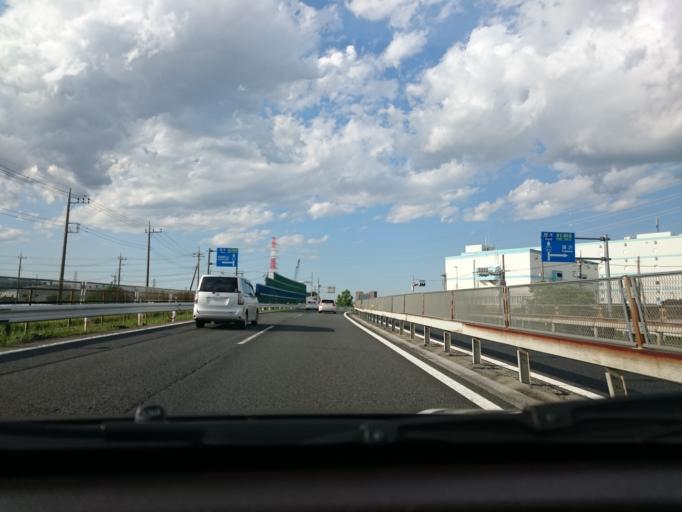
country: JP
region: Kanagawa
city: Isehara
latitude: 35.4016
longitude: 139.3351
